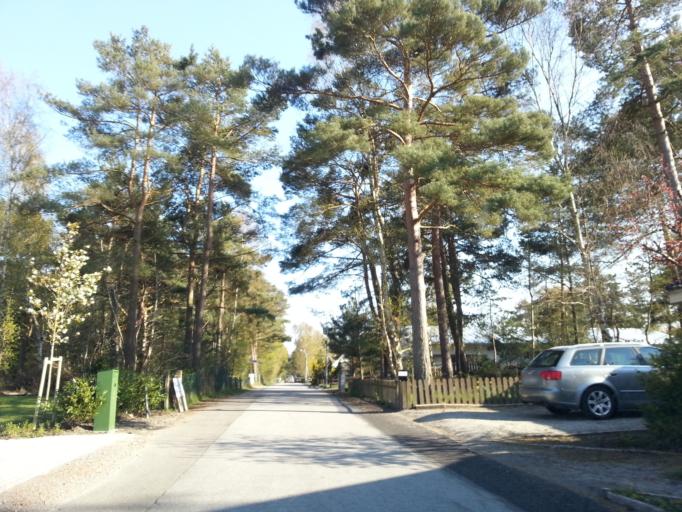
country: SE
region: Skane
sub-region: Vellinge Kommun
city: Hollviken
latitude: 55.4126
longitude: 12.9485
